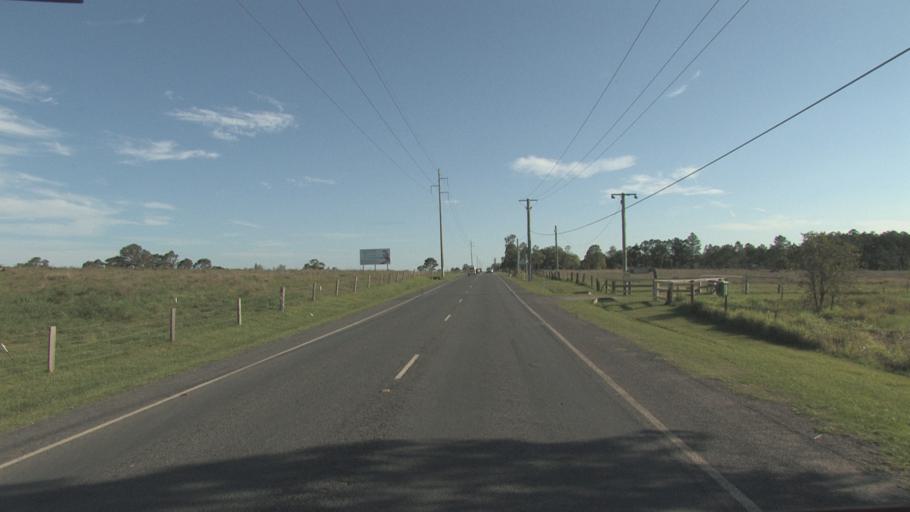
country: AU
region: Queensland
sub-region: Logan
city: Waterford West
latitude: -27.7047
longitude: 153.1173
